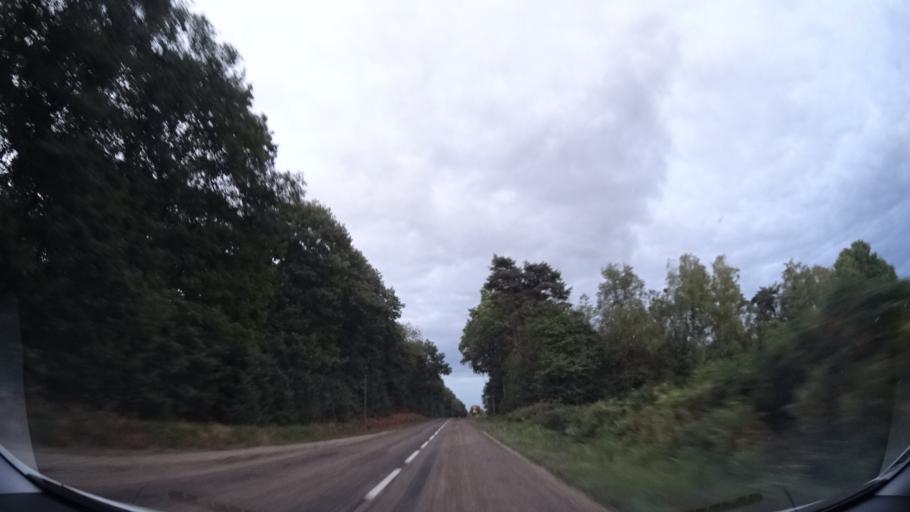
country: FR
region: Bourgogne
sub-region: Departement de l'Yonne
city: Aillant-sur-Tholon
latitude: 47.9201
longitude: 3.3057
